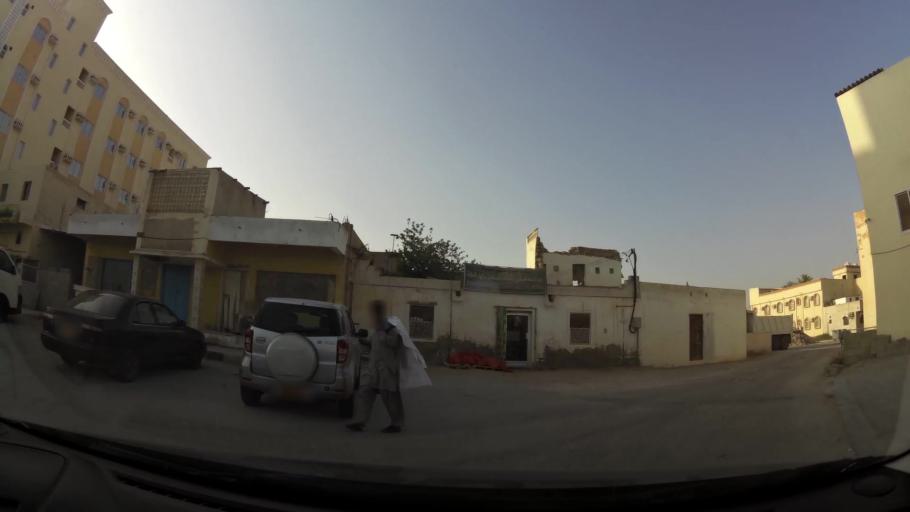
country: OM
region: Zufar
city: Salalah
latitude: 17.0093
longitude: 54.0920
